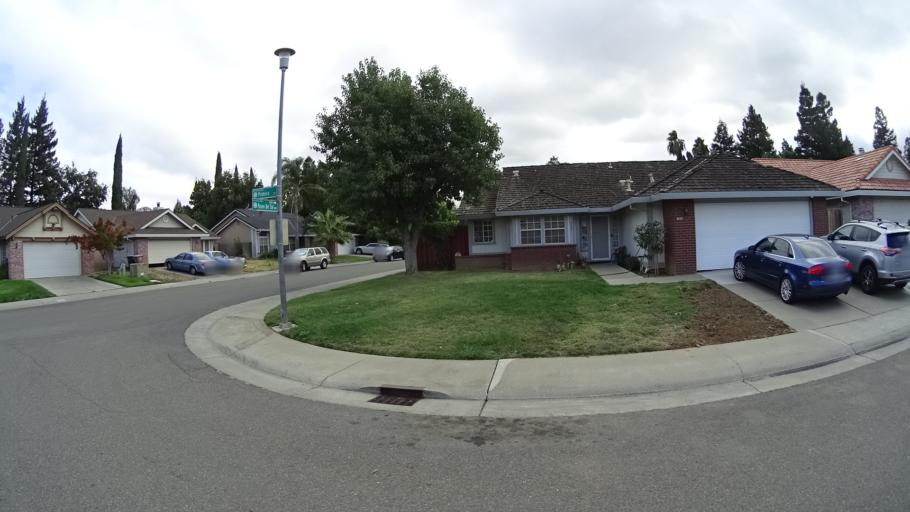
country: US
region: California
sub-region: Sacramento County
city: Laguna
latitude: 38.4227
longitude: -121.4294
